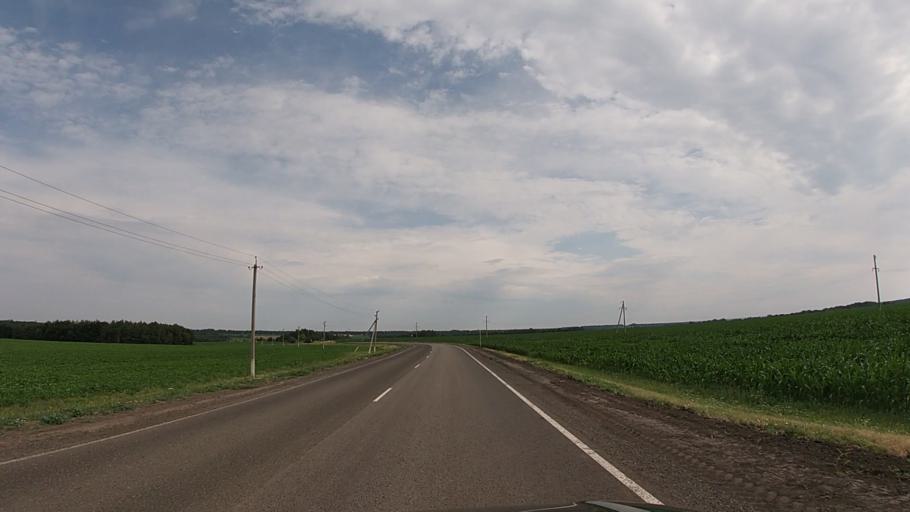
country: RU
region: Belgorod
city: Krasnaya Yaruga
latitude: 50.8189
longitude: 35.5019
